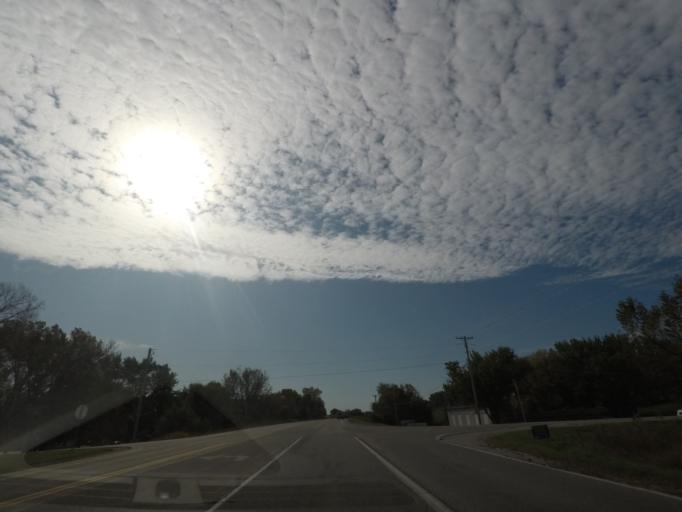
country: US
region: Iowa
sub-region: Story County
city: Gilbert
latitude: 42.0782
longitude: -93.6208
